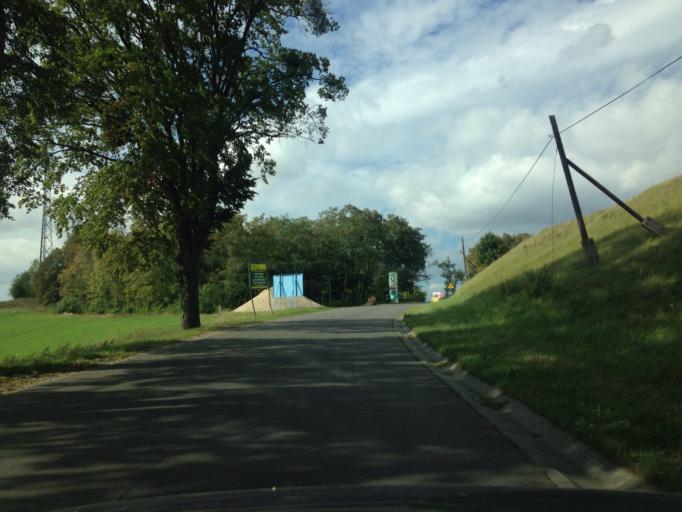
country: PL
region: Kujawsko-Pomorskie
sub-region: Powiat brodnicki
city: Gorzno
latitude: 53.2016
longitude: 19.6398
